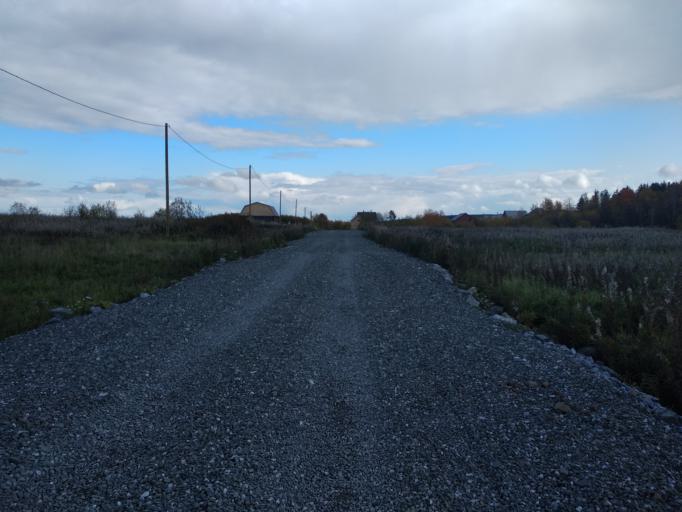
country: RU
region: Sverdlovsk
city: Krasnotur'insk
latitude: 59.7641
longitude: 60.1426
